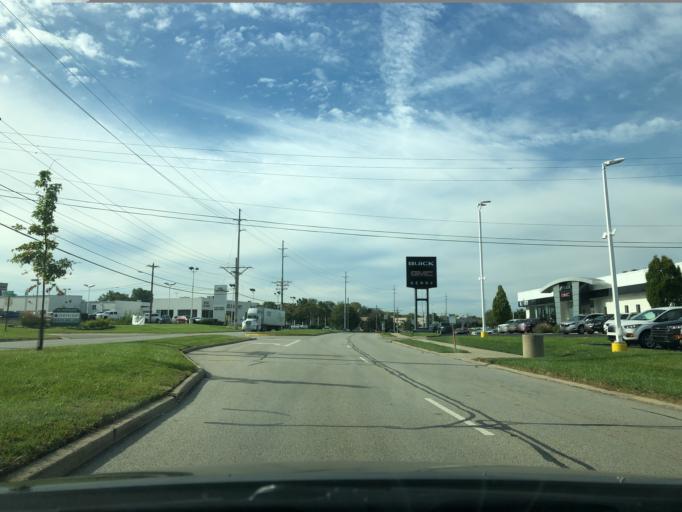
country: US
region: Ohio
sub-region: Hamilton County
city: Springdale
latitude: 39.2854
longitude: -84.4743
